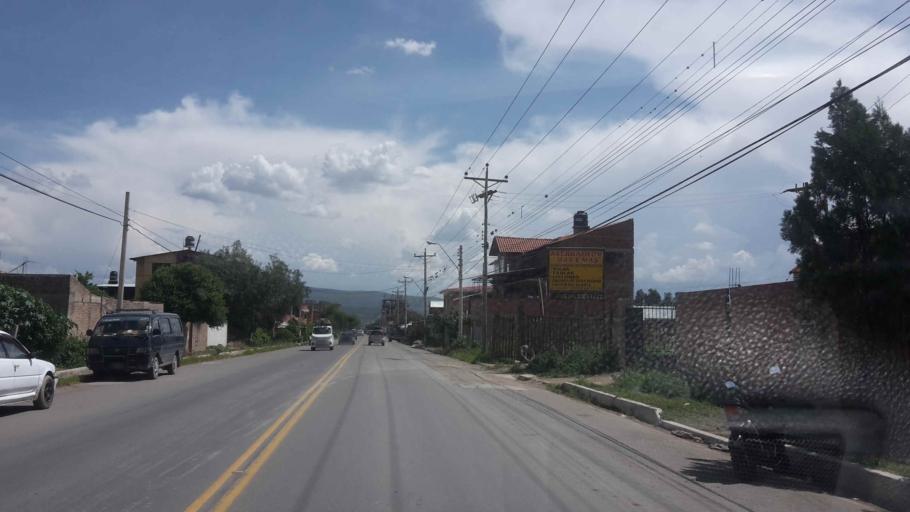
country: BO
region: Cochabamba
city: Cochabamba
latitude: -17.3741
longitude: -66.2333
